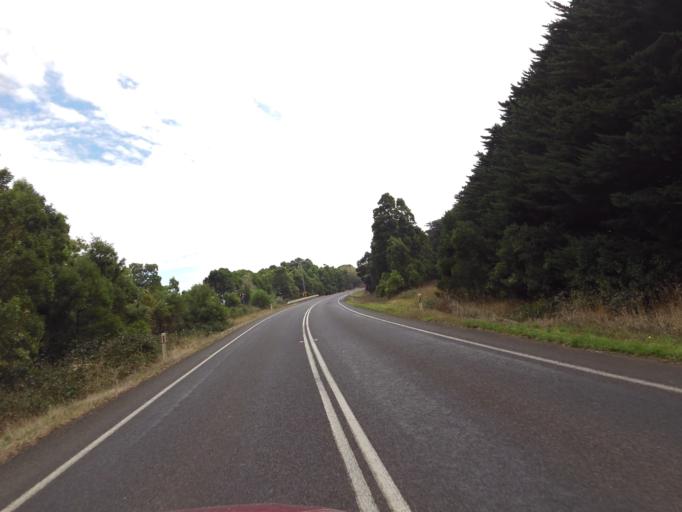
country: AU
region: Victoria
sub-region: Warrnambool
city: Allansford
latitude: -38.3272
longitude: 143.0280
